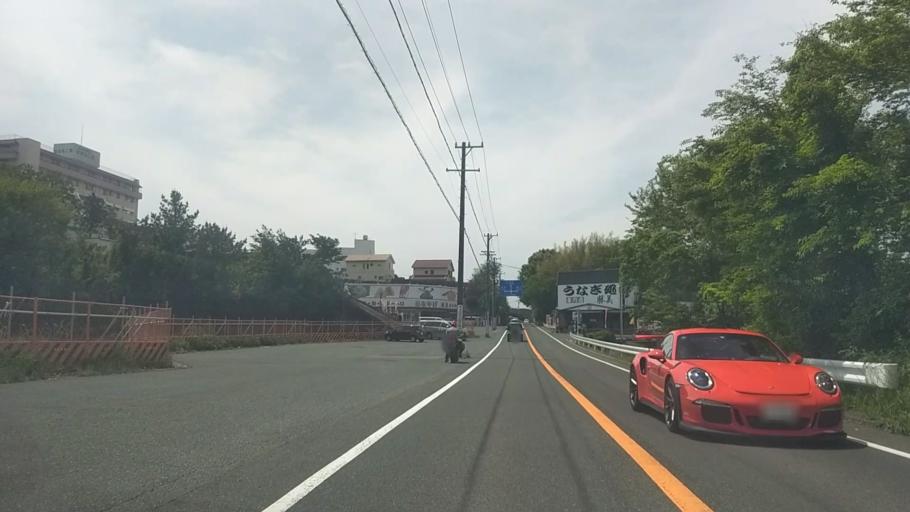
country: JP
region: Shizuoka
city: Kosai-shi
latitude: 34.7964
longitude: 137.5848
